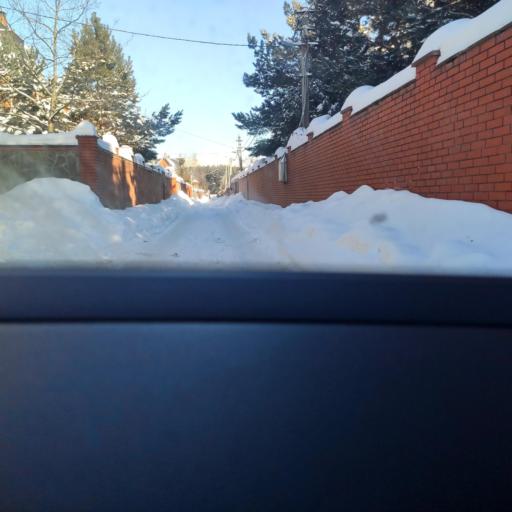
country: RU
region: Moskovskaya
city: Mosrentgen
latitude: 55.6296
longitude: 37.4609
